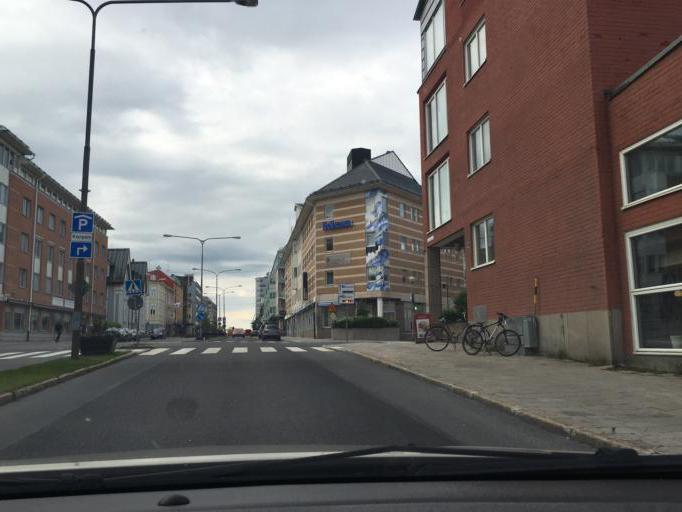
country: SE
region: Norrbotten
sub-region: Lulea Kommun
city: Lulea
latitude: 65.5818
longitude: 22.1538
